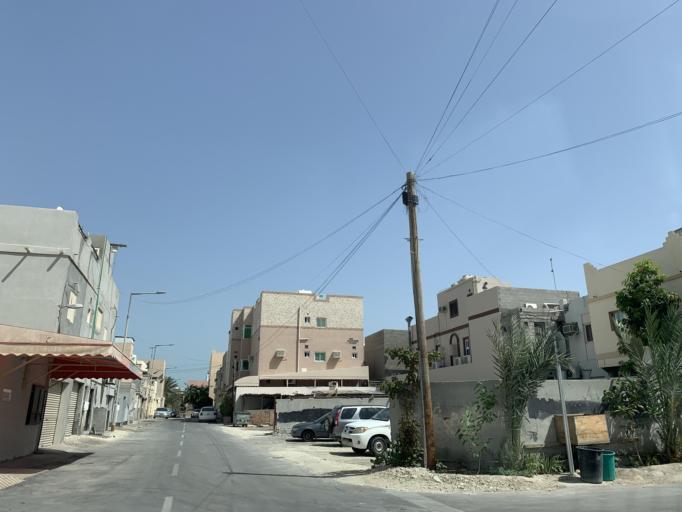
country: BH
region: Northern
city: Sitrah
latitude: 26.1416
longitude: 50.6059
